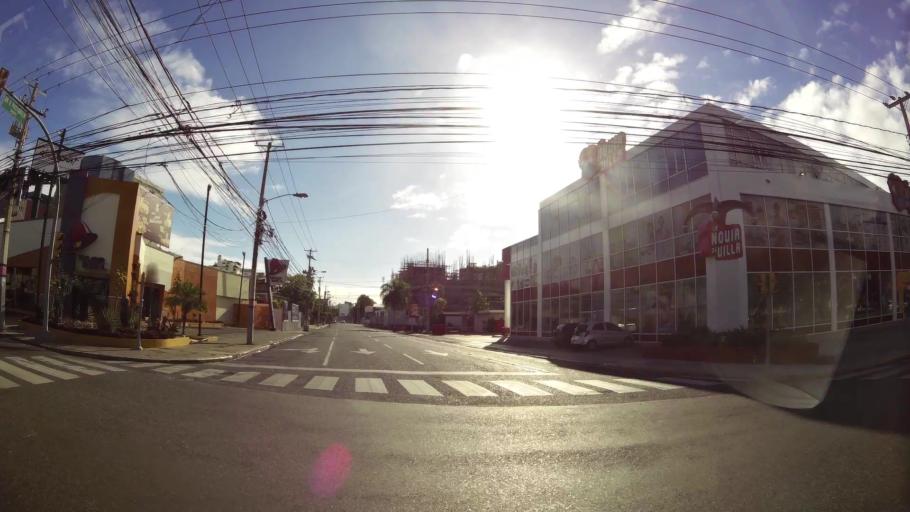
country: DO
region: Nacional
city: La Julia
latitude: 18.4693
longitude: -69.9316
